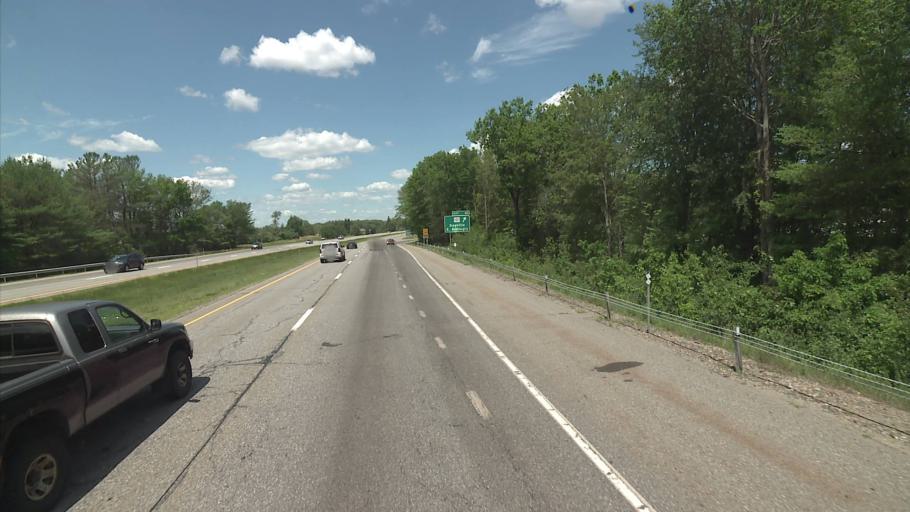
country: US
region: Connecticut
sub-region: Windham County
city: Killingly Center
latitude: 41.8389
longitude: -71.8772
